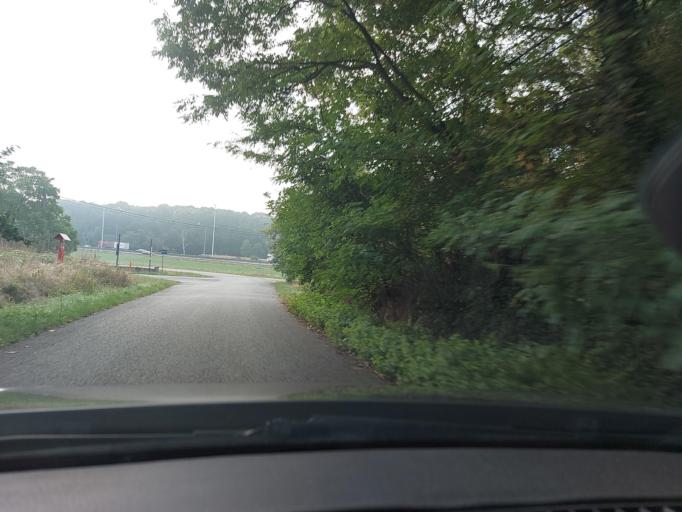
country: BE
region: Flanders
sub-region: Provincie Antwerpen
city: Laakdal
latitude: 51.1068
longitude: 5.0319
